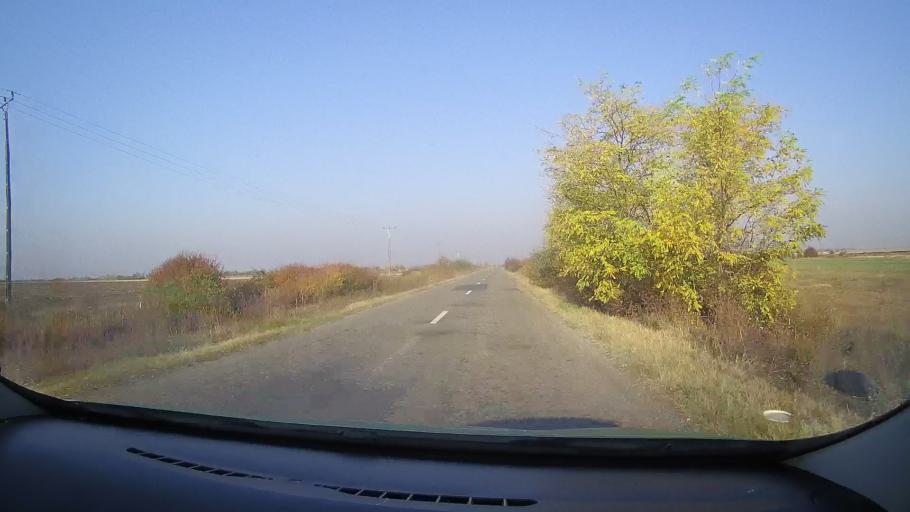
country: RO
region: Arad
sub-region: Comuna Graniceri
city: Graniceri
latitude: 46.5071
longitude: 21.3229
